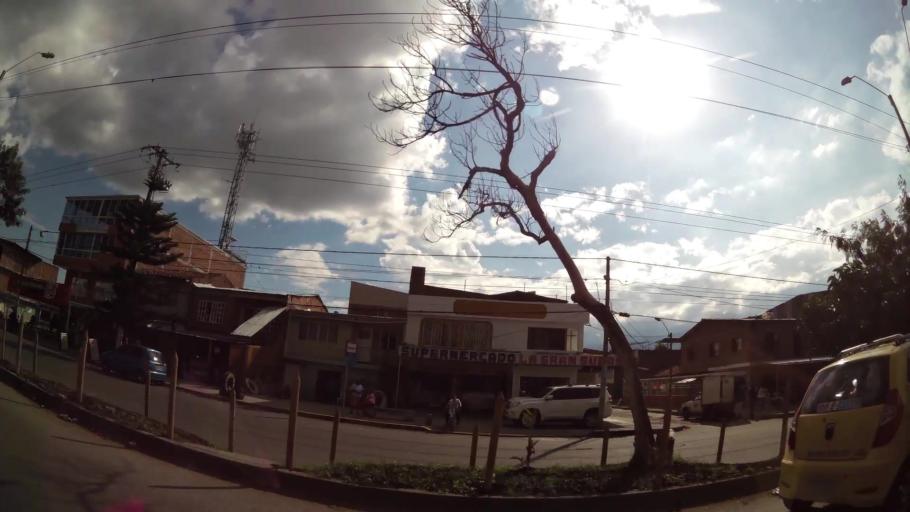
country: CO
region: Valle del Cauca
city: Cali
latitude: 3.4133
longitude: -76.5022
